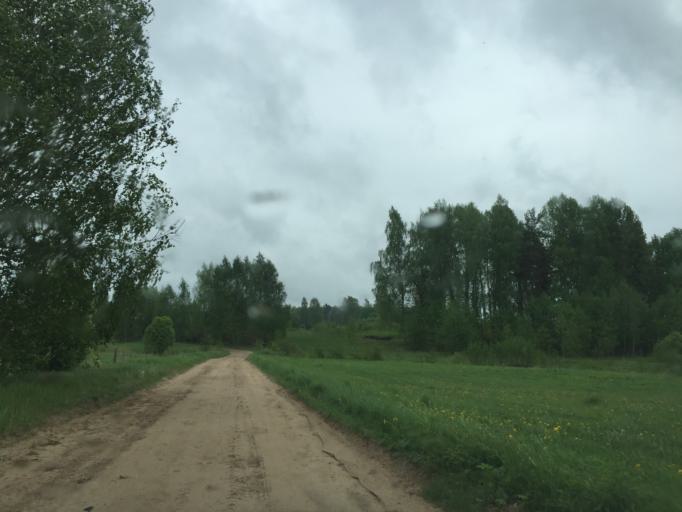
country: LV
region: Kegums
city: Kegums
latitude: 56.7352
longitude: 24.7452
